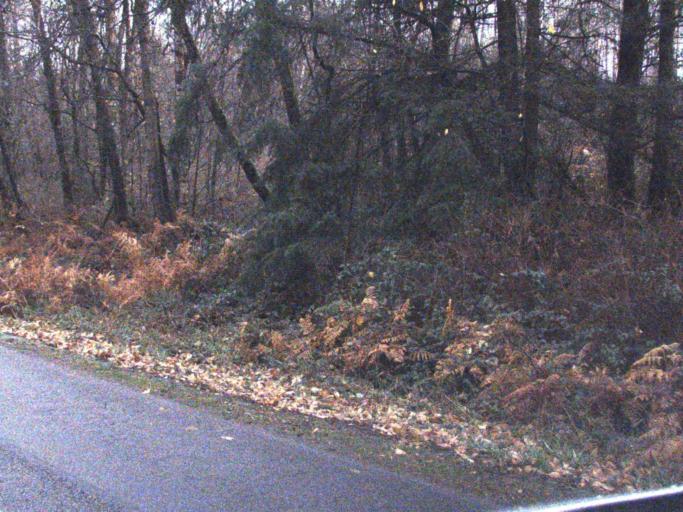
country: US
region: Washington
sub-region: Snohomish County
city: Sisco Heights
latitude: 48.1211
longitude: -122.1125
